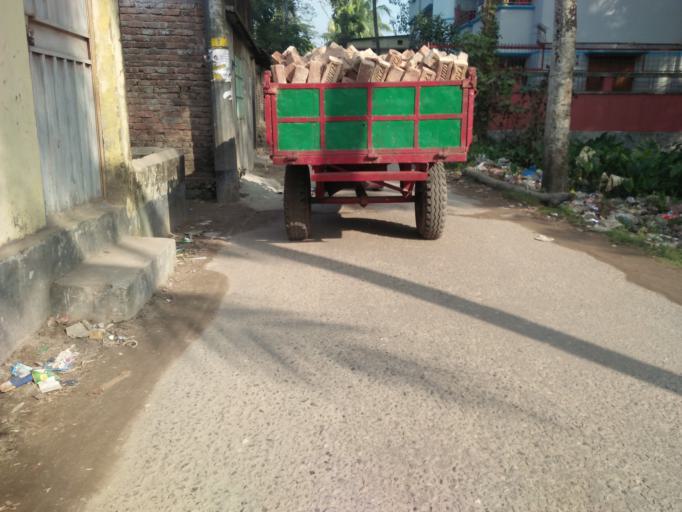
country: BD
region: Barisal
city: Bhola
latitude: 22.6812
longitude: 90.6425
